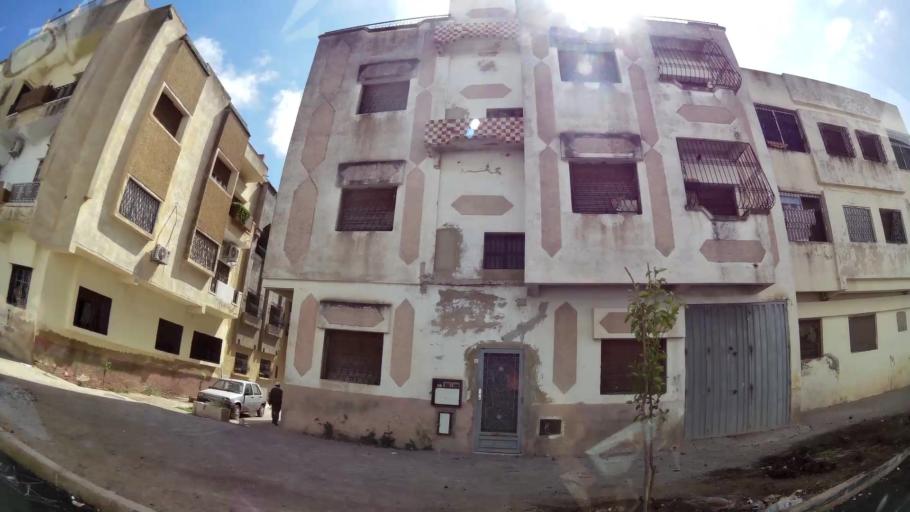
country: MA
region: Fes-Boulemane
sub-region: Fes
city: Fes
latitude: 34.0391
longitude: -5.0321
